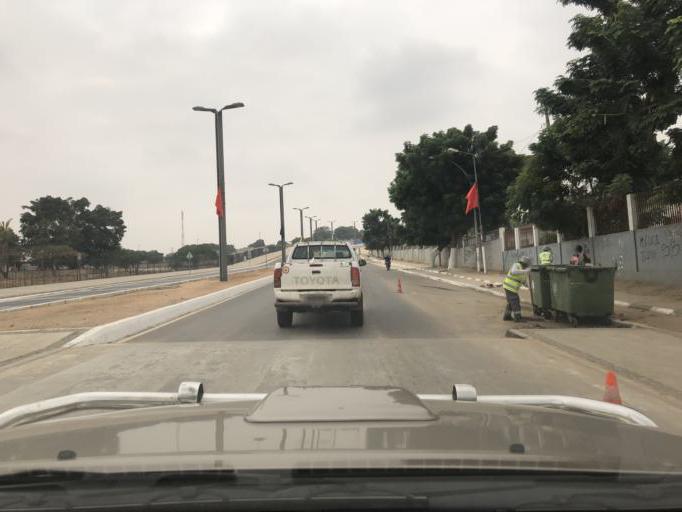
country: AO
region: Luanda
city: Luanda
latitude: -8.9082
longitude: 13.1693
